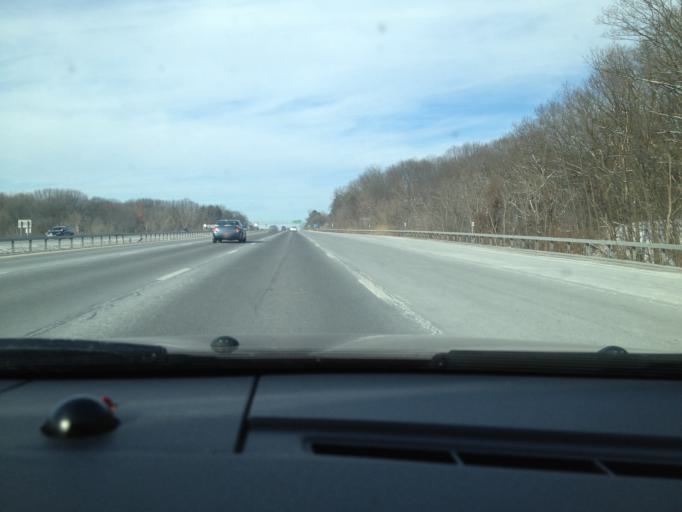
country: US
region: New York
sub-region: Albany County
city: Albany
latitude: 42.6713
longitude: -73.7546
